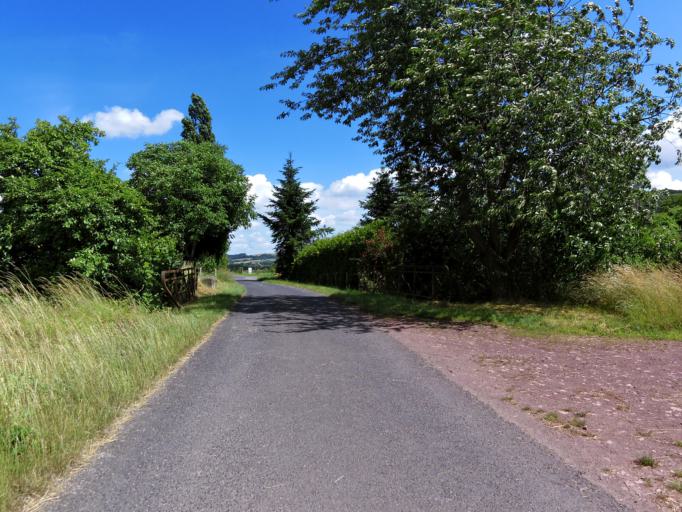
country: DE
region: Hesse
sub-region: Regierungsbezirk Kassel
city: Herleshausen
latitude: 51.0024
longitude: 10.1713
